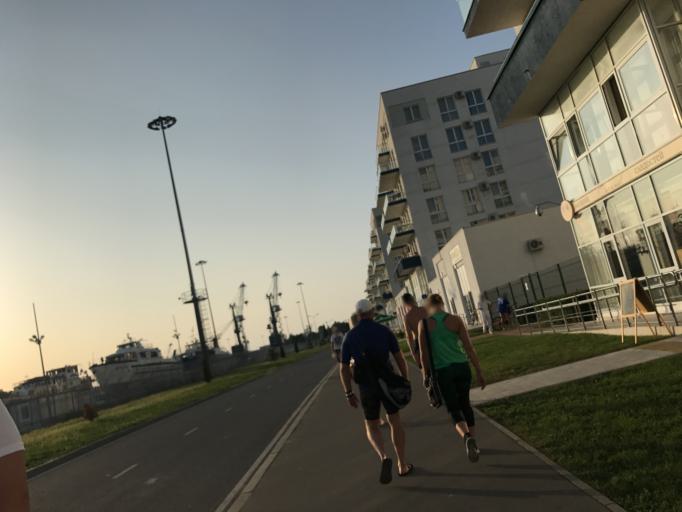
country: RU
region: Krasnodarskiy
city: Adler
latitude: 43.4114
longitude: 39.9349
